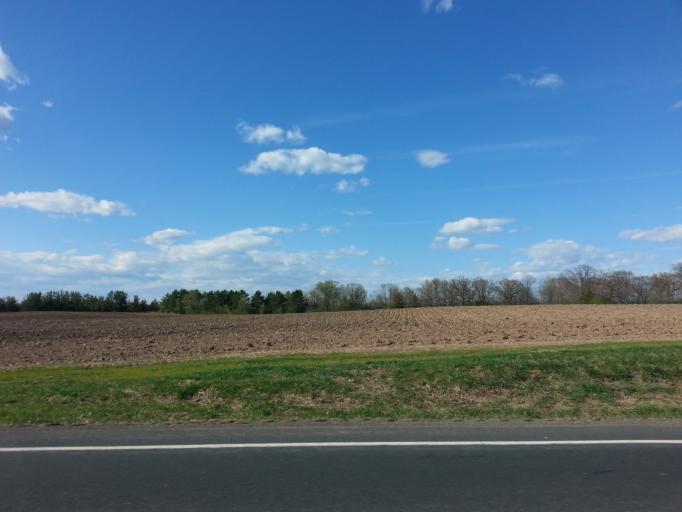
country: US
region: Minnesota
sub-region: Washington County
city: Stillwater
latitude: 45.0606
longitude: -92.7725
